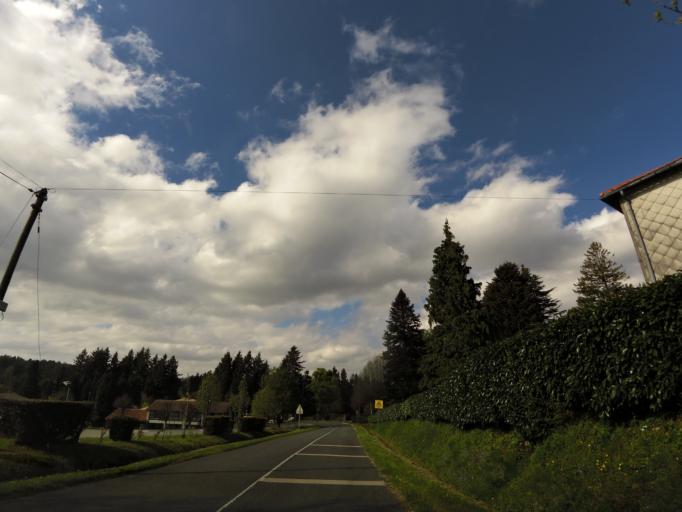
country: FR
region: Midi-Pyrenees
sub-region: Departement du Tarn
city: Soreze
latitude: 43.4079
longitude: 2.0811
